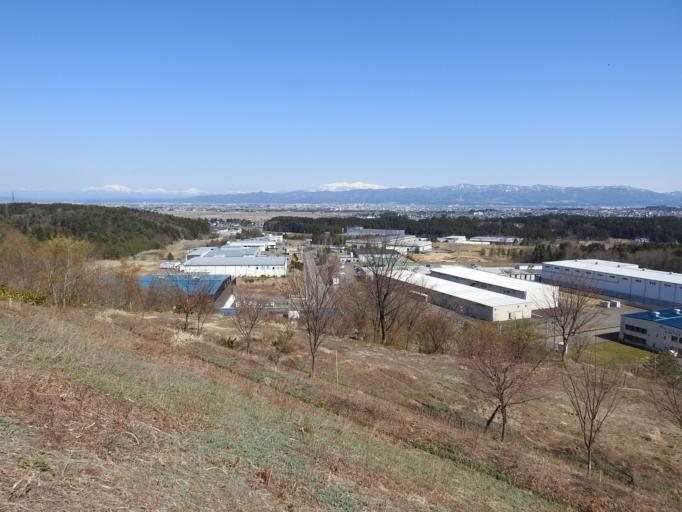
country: JP
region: Niigata
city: Nagaoka
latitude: 37.4664
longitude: 138.7451
